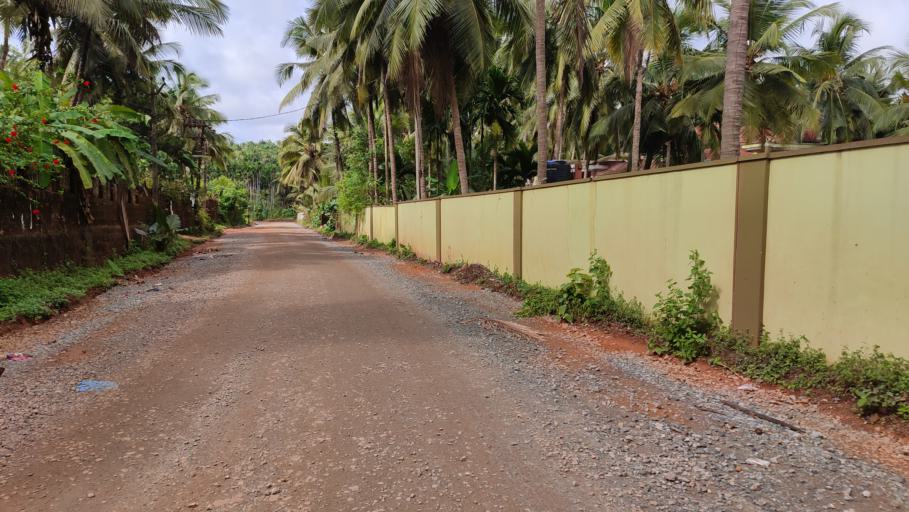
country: IN
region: Kerala
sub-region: Kasaragod District
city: Kasaragod
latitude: 12.5190
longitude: 75.0719
